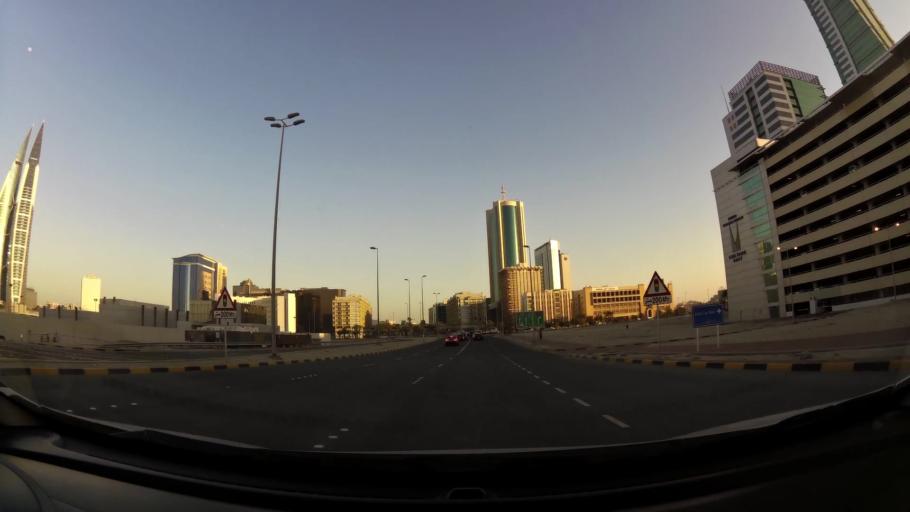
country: BH
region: Manama
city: Manama
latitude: 26.2396
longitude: 50.5757
